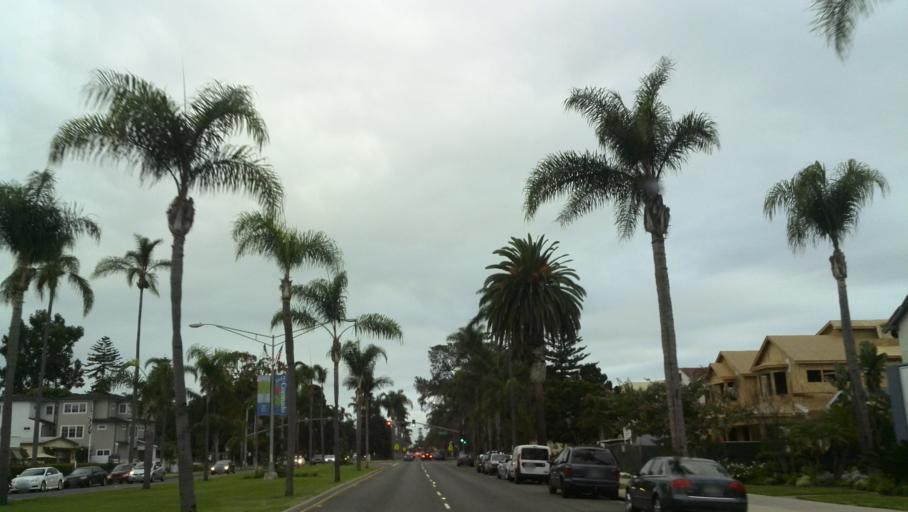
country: US
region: California
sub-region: San Diego County
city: Coronado
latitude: 32.6929
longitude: -117.1759
